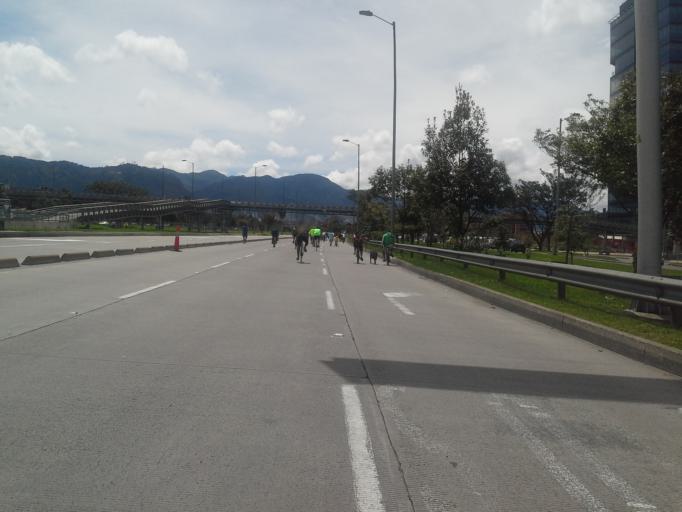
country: CO
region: Bogota D.C.
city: Bogota
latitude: 4.6467
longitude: -74.0991
